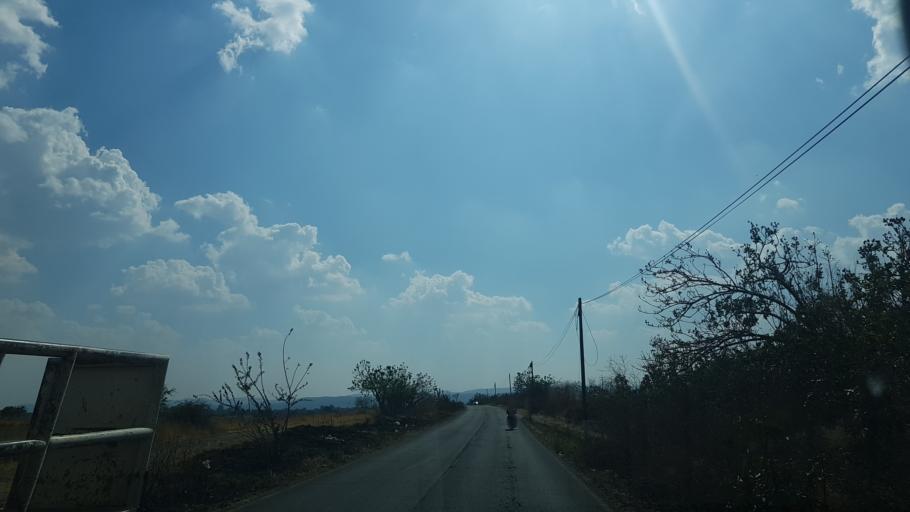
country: MX
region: Puebla
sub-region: Atlixco
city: Colonia Agricola de Ocotepec (Colonia San Jose)
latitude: 18.8989
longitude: -98.4990
